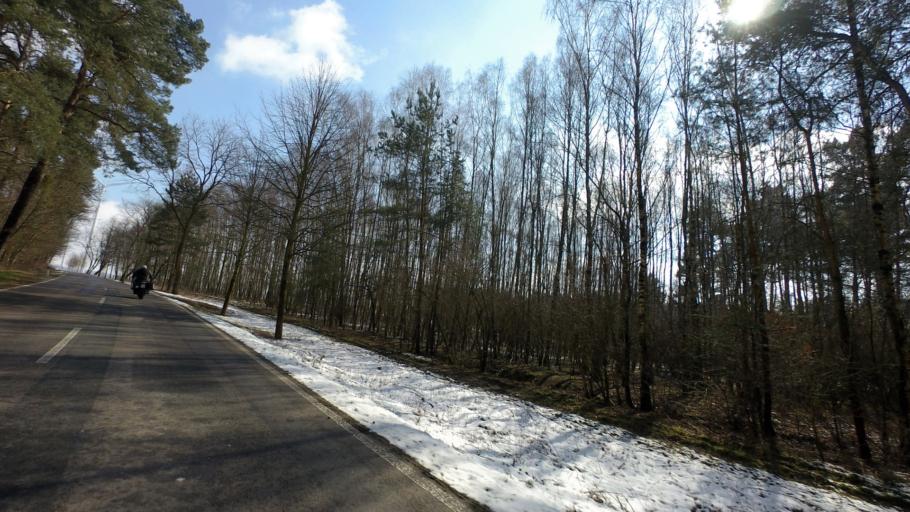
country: DE
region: Brandenburg
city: Rudnitz
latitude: 52.6972
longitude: 13.6759
